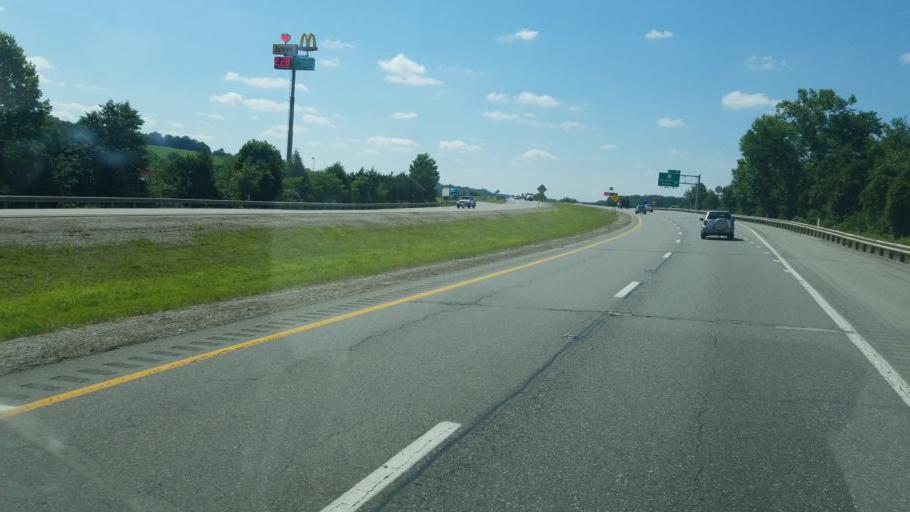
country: US
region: West Virginia
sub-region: Jackson County
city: Ripley
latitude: 38.7578
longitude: -81.6874
